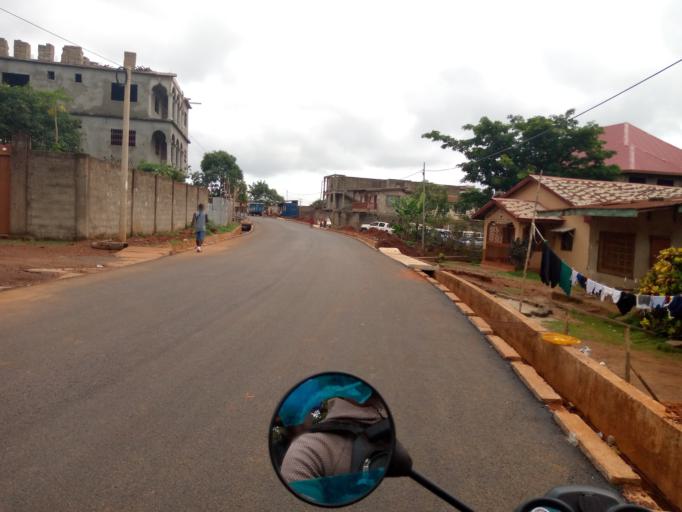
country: SL
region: Western Area
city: Hastings
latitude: 8.4096
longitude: -13.1433
